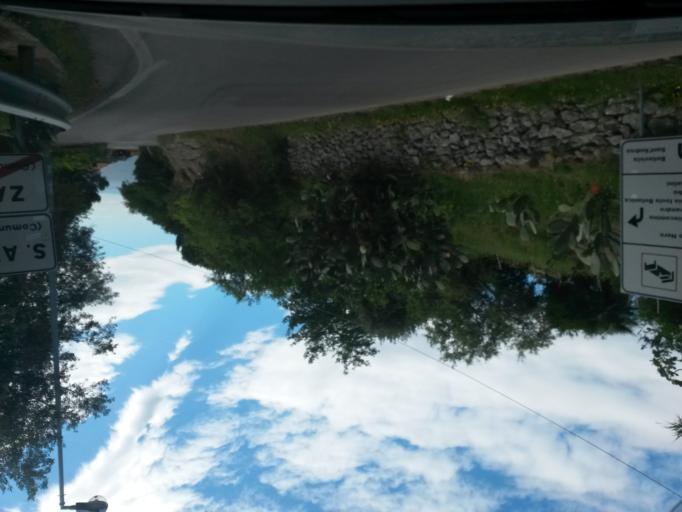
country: IT
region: Tuscany
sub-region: Provincia di Livorno
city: Marciana
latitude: 42.8020
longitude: 10.1366
